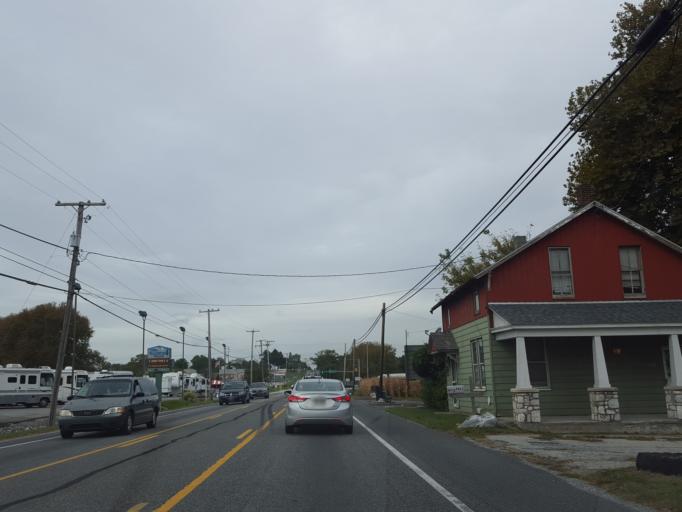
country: US
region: Pennsylvania
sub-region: York County
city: Weigelstown
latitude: 39.9286
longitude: -76.8349
